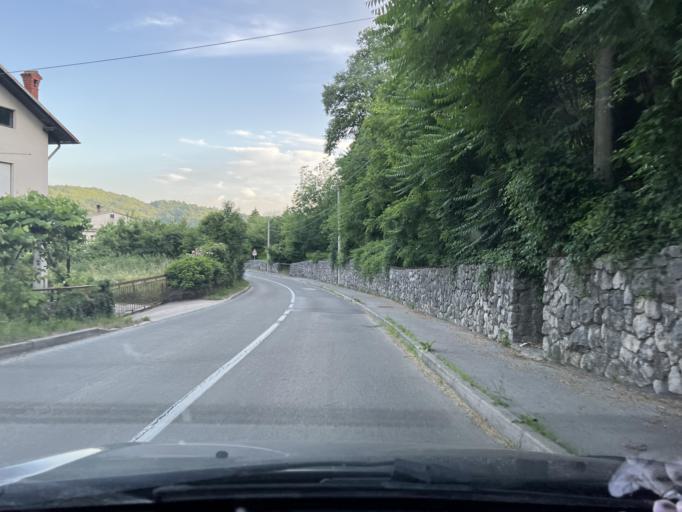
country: HR
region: Primorsko-Goranska
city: Drazice
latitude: 45.3863
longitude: 14.4488
